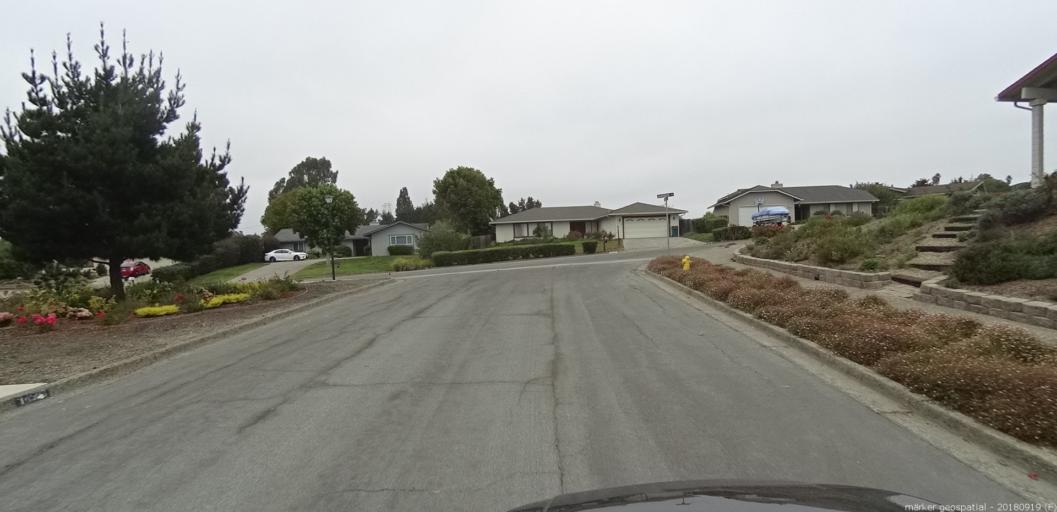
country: US
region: California
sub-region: Monterey County
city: Castroville
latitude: 36.7782
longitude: -121.7242
